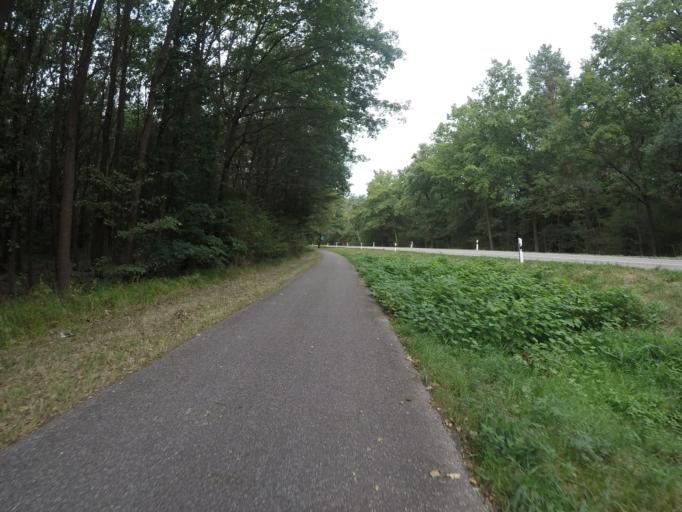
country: DE
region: Rheinland-Pfalz
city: Hanhofen
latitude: 49.3493
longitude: 8.3547
